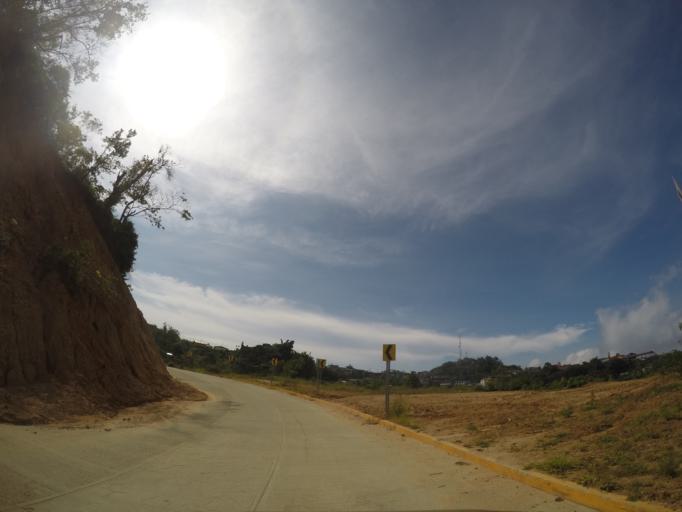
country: MX
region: Oaxaca
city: Pluma Hidalgo
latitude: 15.9301
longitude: -96.4197
